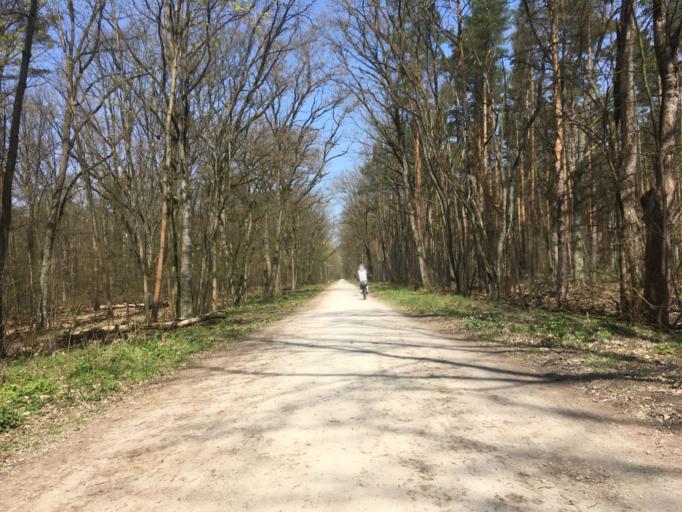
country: DE
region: Berlin
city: Grunewald
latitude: 52.4718
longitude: 13.2356
